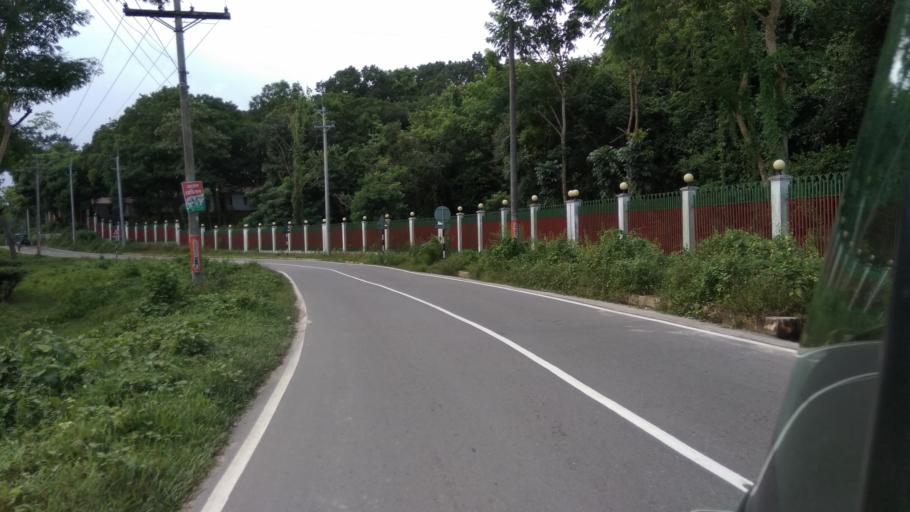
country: IN
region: Tripura
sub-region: Dhalai
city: Kamalpur
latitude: 24.2993
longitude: 91.7609
